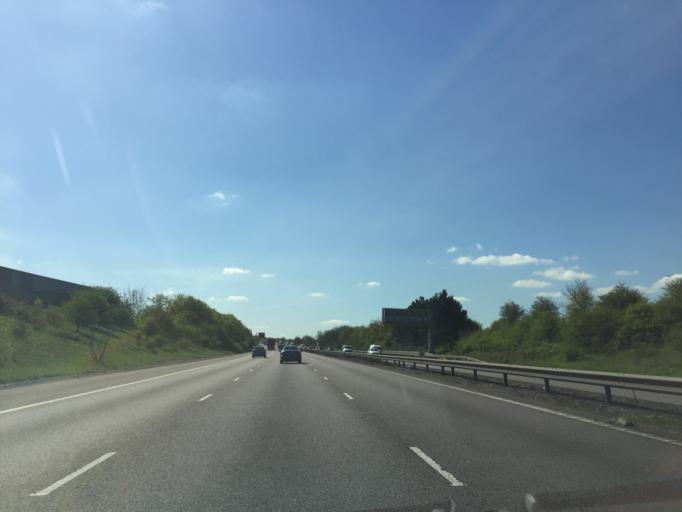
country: GB
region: England
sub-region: Essex
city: Epping
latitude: 51.7213
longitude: 0.1422
